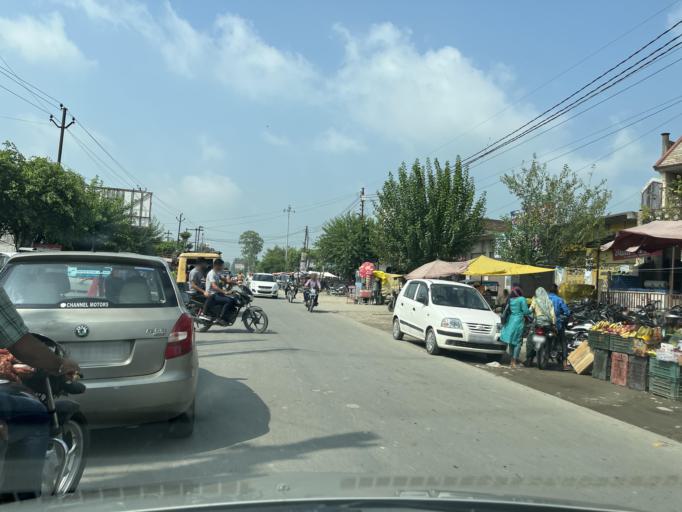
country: IN
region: Uttarakhand
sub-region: Udham Singh Nagar
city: Bazpur
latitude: 29.1538
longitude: 79.1448
